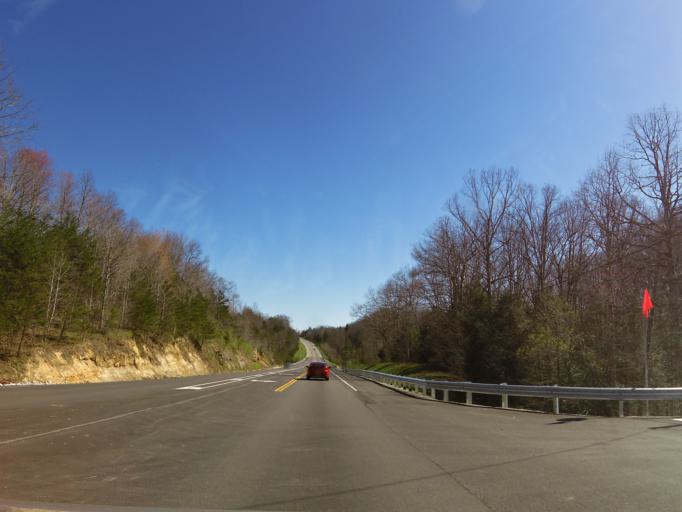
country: US
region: Kentucky
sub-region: McCreary County
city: Whitley City
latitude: 36.7151
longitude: -84.4647
